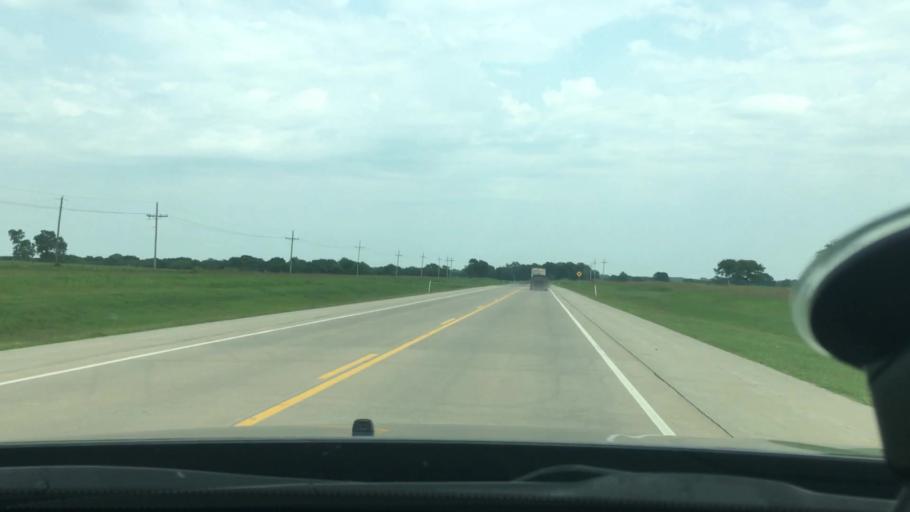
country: US
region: Oklahoma
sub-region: Pontotoc County
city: Ada
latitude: 34.6519
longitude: -96.8164
